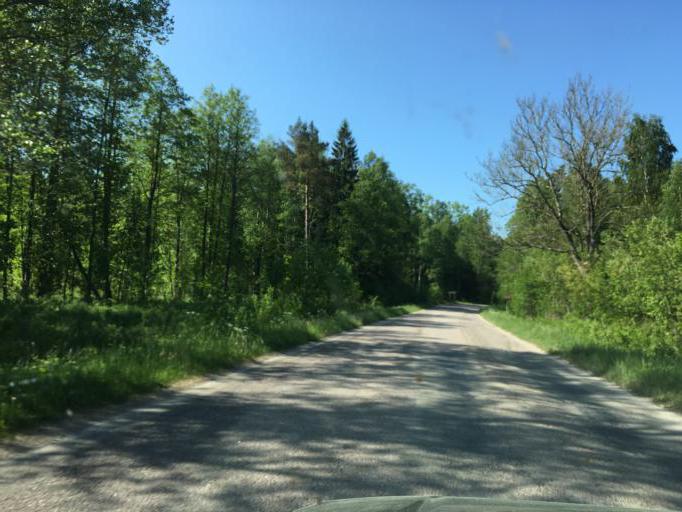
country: LV
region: Ventspils
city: Ventspils
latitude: 57.4935
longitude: 21.8094
